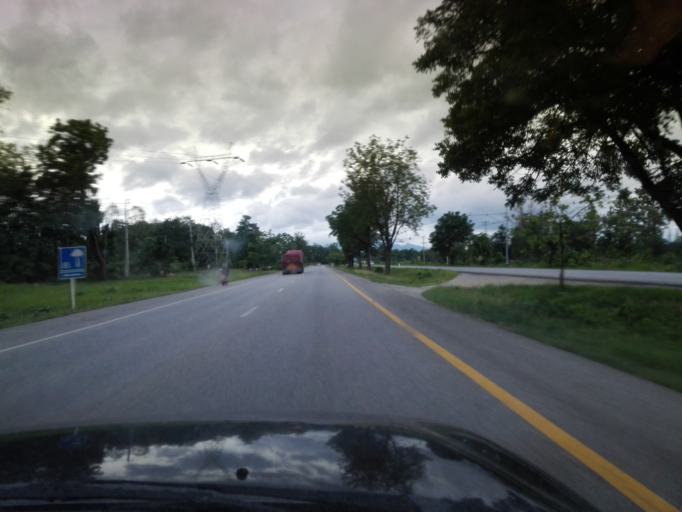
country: TH
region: Tak
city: Tak
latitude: 16.7975
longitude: 99.1541
